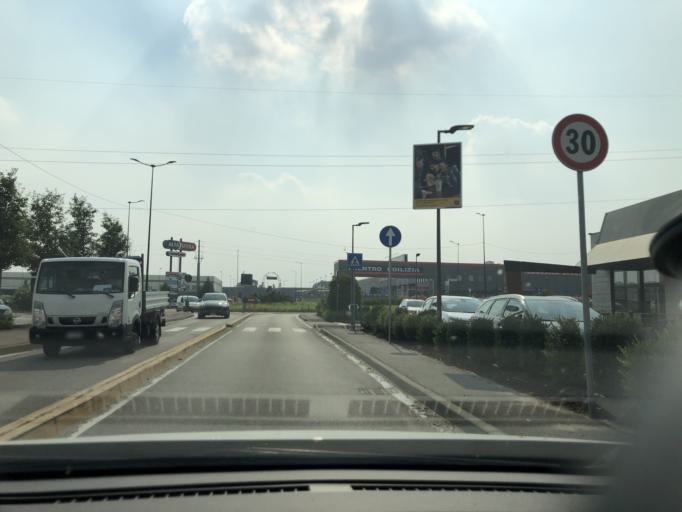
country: IT
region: Lombardy
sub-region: Citta metropolitana di Milano
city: Novegro-Tregarezzo-San Felice
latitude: 45.4861
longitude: 9.2642
